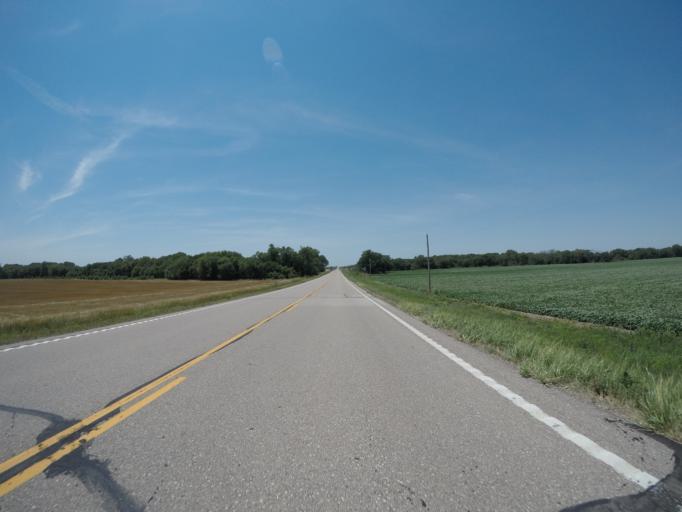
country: US
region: Kansas
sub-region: Dickinson County
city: Solomon
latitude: 39.0308
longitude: -97.4677
